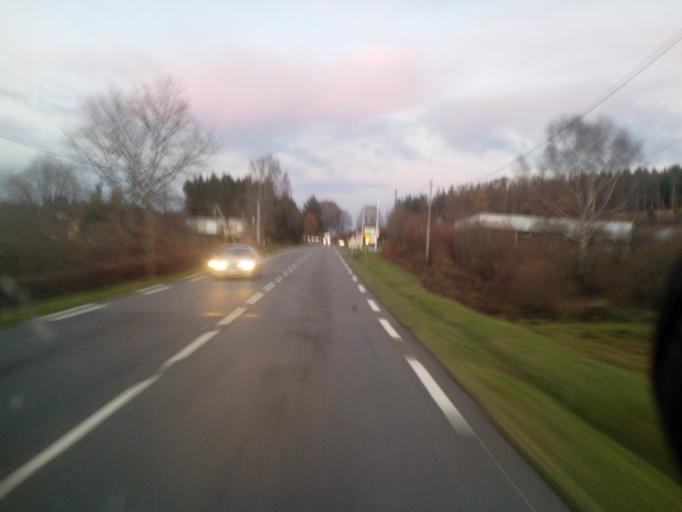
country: FR
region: Limousin
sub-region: Departement de la Correze
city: Ussel
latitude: 45.5079
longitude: 2.2450
